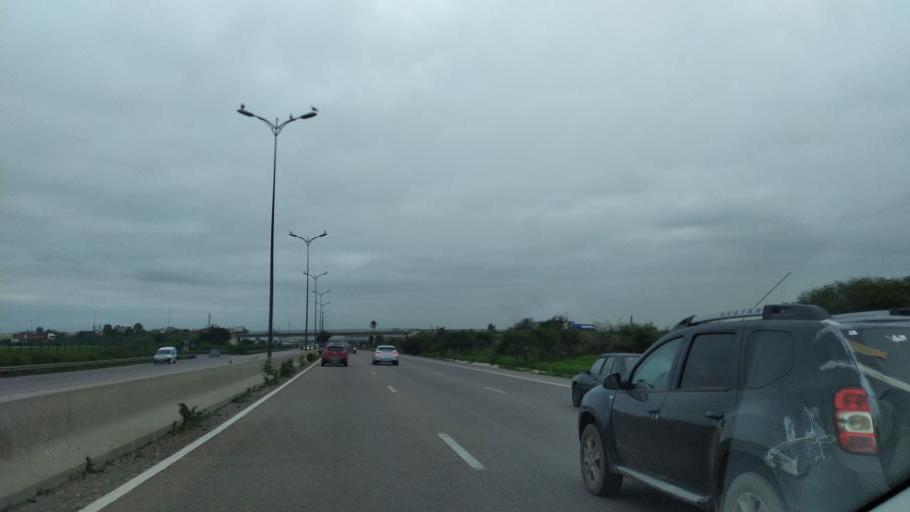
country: MA
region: Grand Casablanca
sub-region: Mediouna
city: Tit Mellil
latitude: 33.6303
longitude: -7.4546
